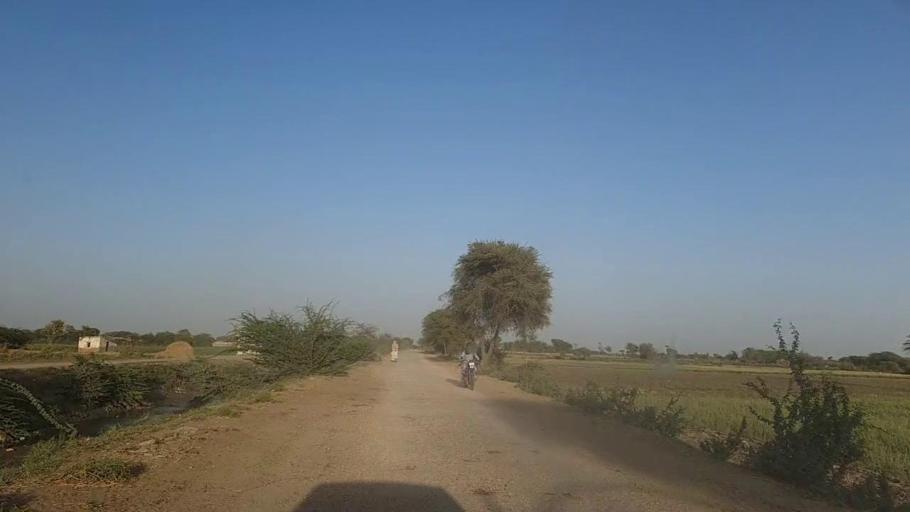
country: PK
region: Sindh
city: Jati
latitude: 24.4145
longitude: 68.3358
